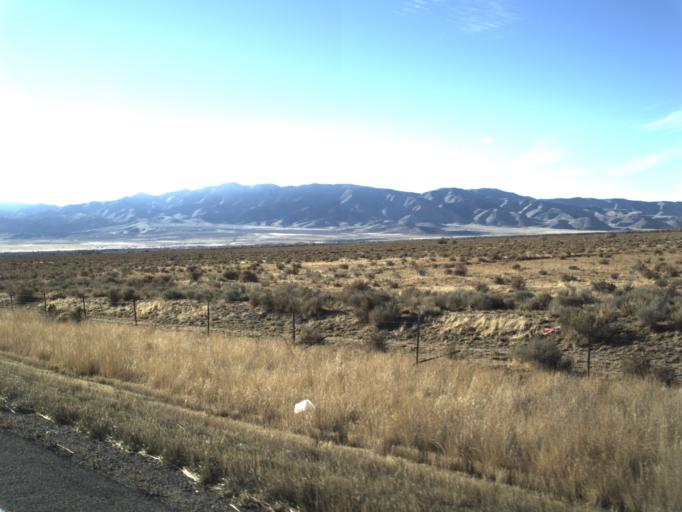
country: US
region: Utah
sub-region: Tooele County
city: Erda
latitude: 40.6138
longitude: -112.3724
